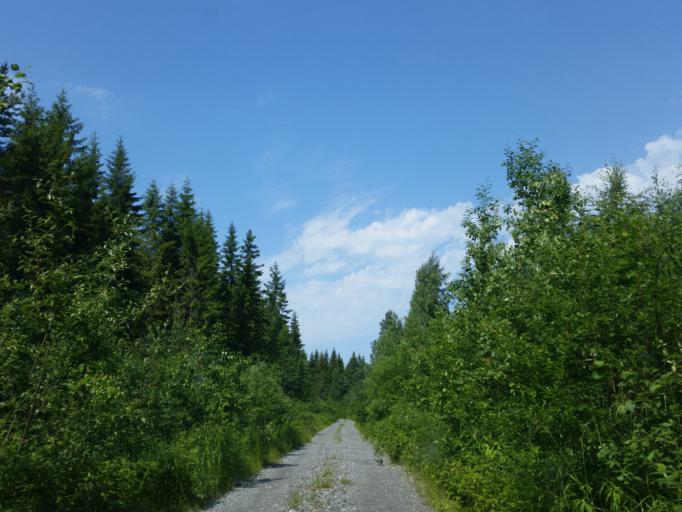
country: FI
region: Northern Savo
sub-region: Ylae-Savo
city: Keitele
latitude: 63.1033
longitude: 26.5419
